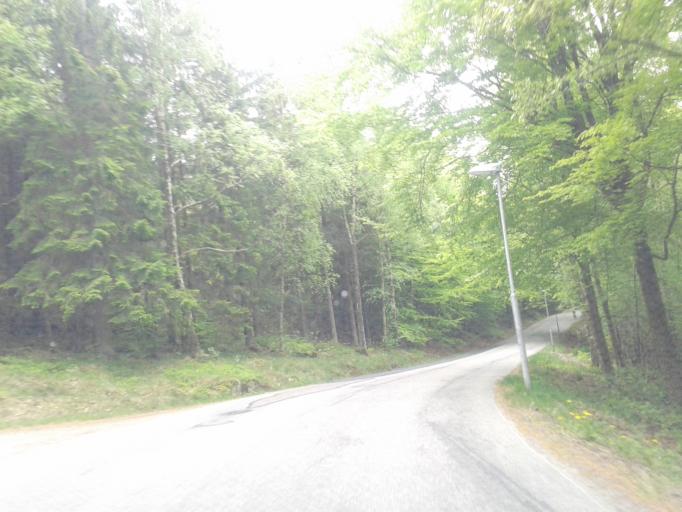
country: SE
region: Vaestra Goetaland
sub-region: Kungalvs Kommun
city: Kungalv
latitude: 57.8754
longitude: 11.9965
